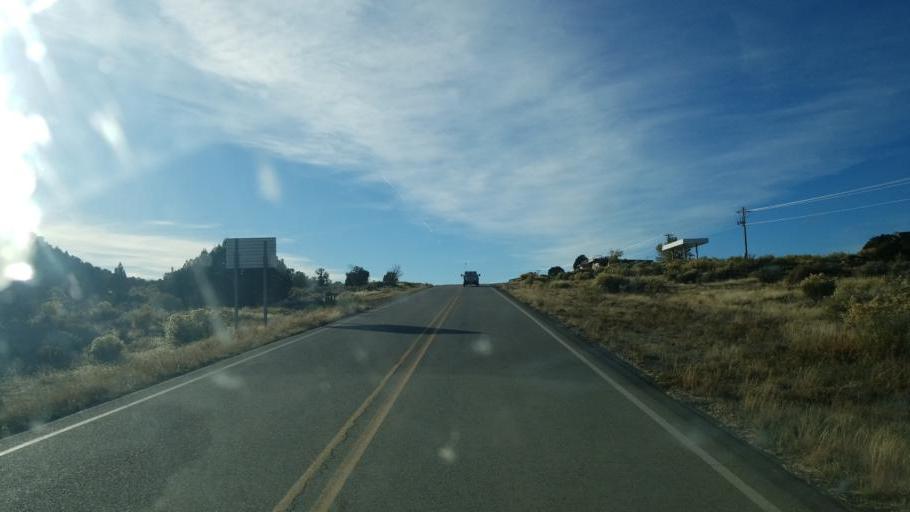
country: US
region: New Mexico
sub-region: San Juan County
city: Bloomfield
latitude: 36.7525
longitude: -107.6044
